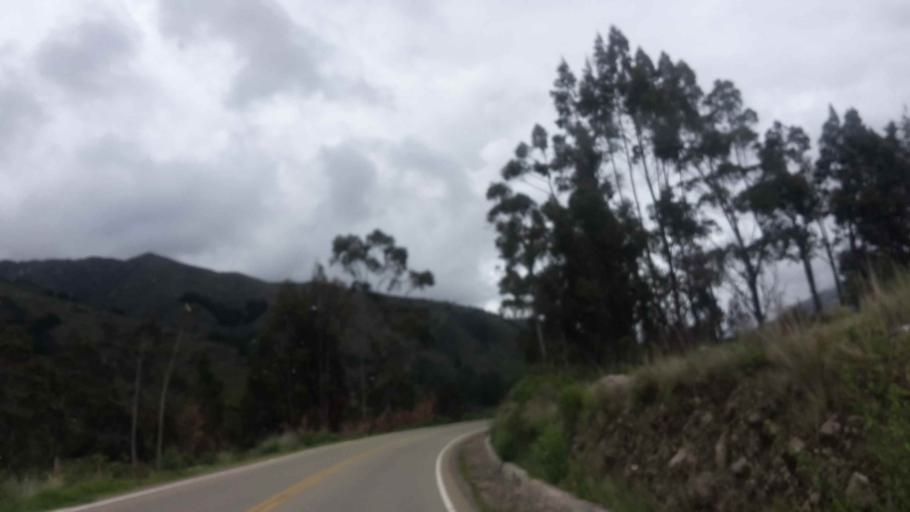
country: BO
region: Cochabamba
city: Arani
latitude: -17.4925
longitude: -65.4567
